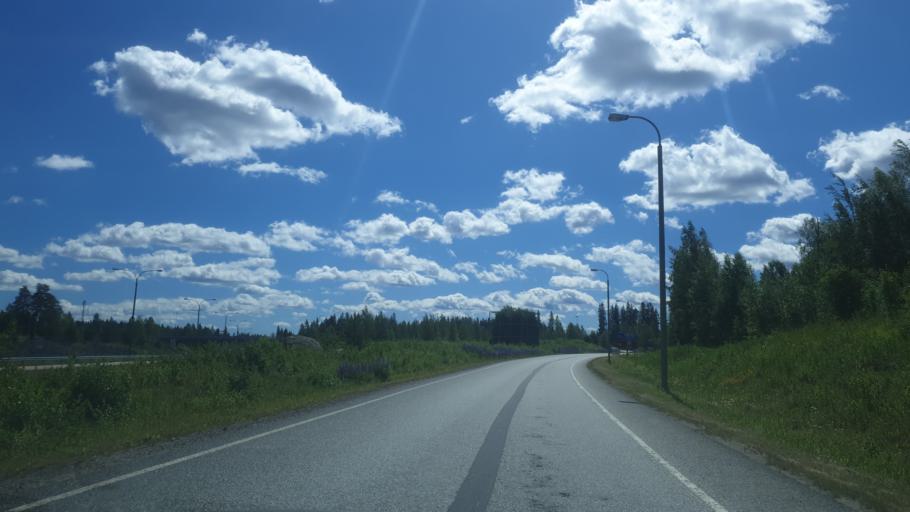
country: FI
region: Northern Savo
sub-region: Varkaus
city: Varkaus
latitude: 62.3334
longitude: 27.8242
